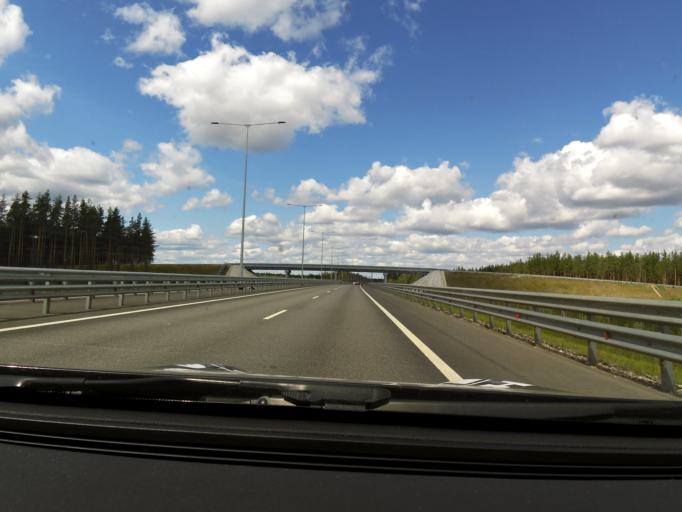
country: RU
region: Tverskaya
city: Krasnomayskiy
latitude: 57.4713
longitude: 34.3521
